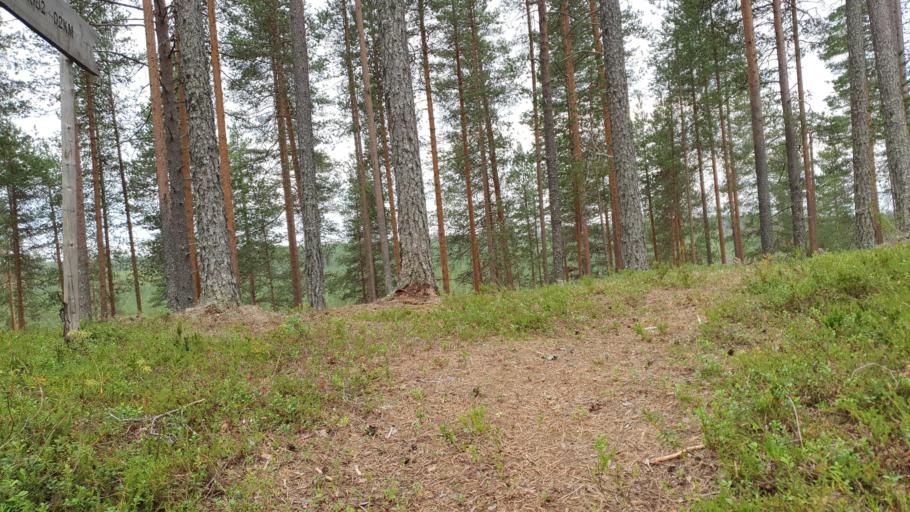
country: RU
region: Republic of Karelia
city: Kostomuksha
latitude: 64.7541
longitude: 29.9848
